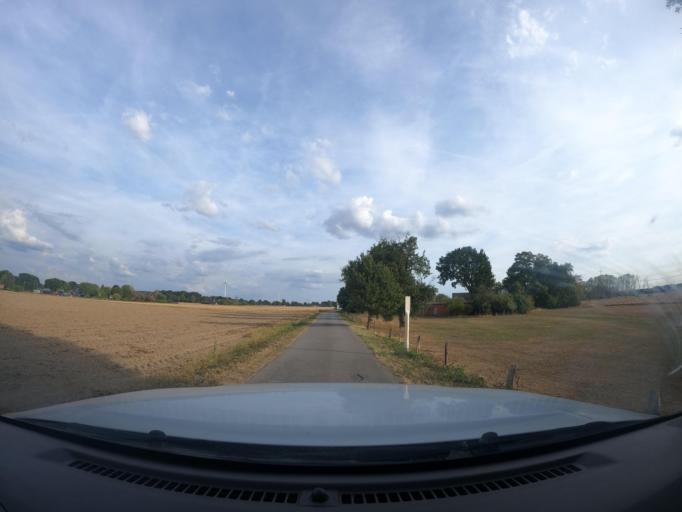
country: DE
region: North Rhine-Westphalia
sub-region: Regierungsbezirk Dusseldorf
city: Hamminkeln
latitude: 51.7154
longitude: 6.5893
